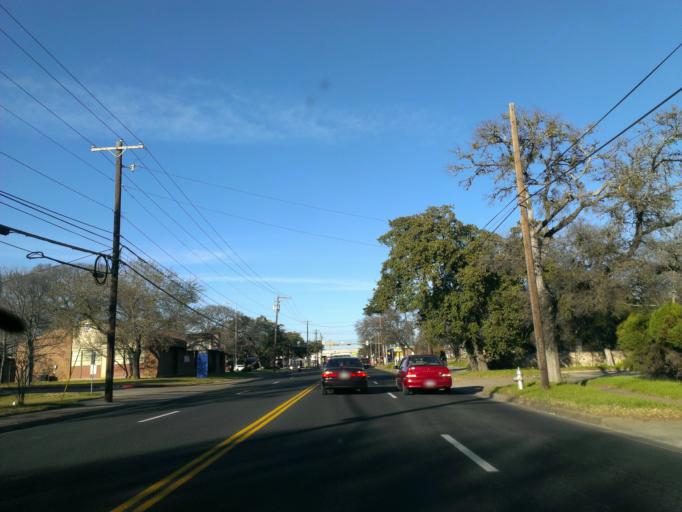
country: US
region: Texas
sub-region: Travis County
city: Rollingwood
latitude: 30.2271
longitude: -97.7901
